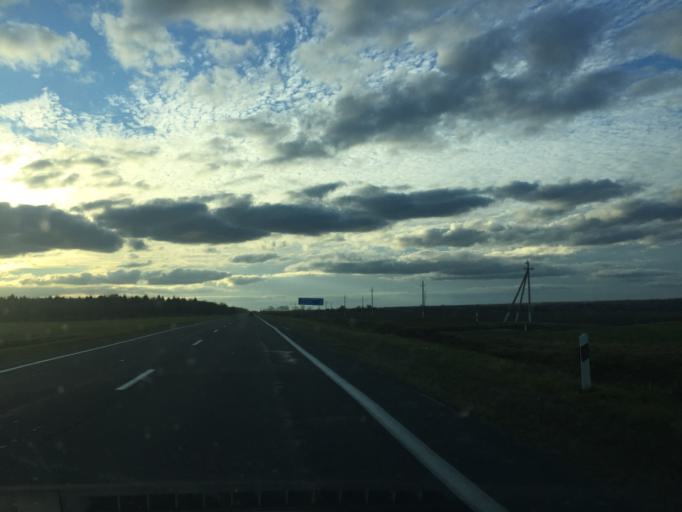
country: BY
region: Vitebsk
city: Vyerkhnyadzvinsk
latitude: 55.8237
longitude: 27.7615
